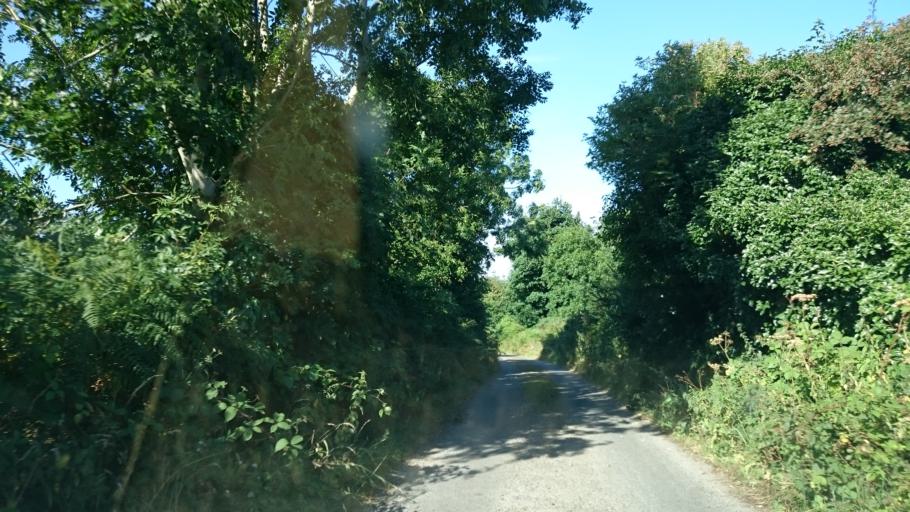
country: IE
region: Leinster
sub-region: Kilkenny
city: Graiguenamanagh
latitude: 52.5250
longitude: -6.9625
